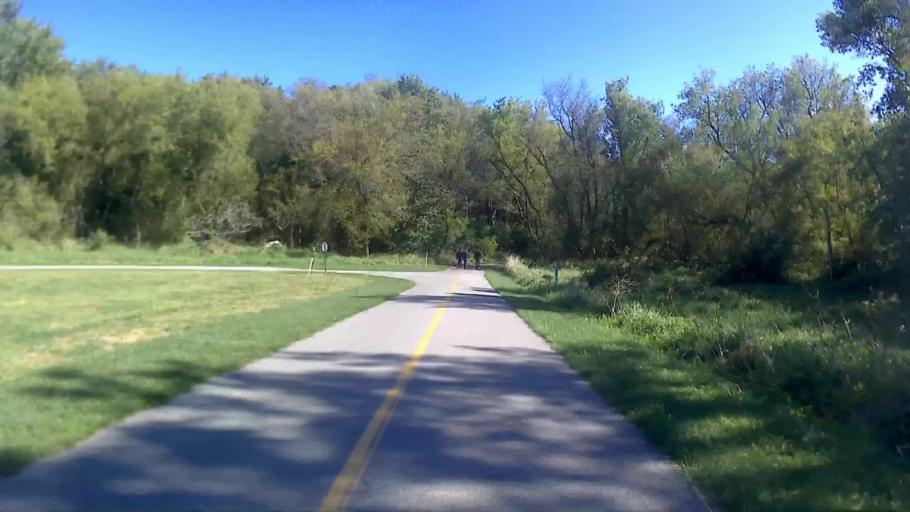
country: US
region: Illinois
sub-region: Cook County
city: Rolling Meadows
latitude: 42.0358
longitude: -88.0236
